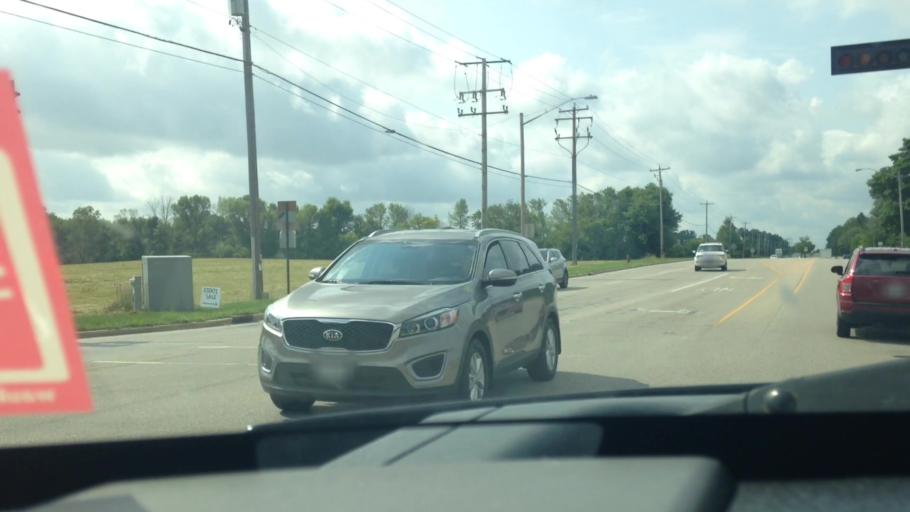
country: US
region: Wisconsin
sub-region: Waukesha County
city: Menomonee Falls
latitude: 43.1486
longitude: -88.1045
